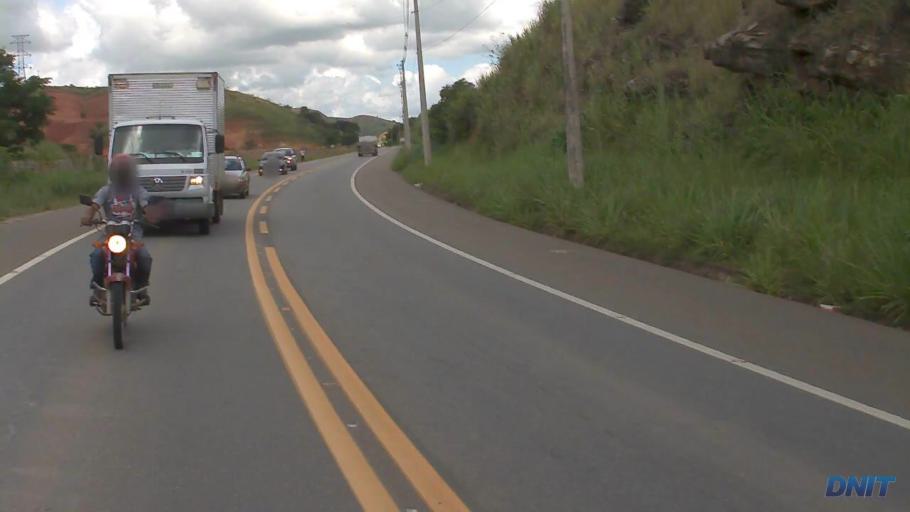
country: BR
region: Minas Gerais
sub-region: Governador Valadares
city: Governador Valadares
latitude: -18.8730
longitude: -41.9923
